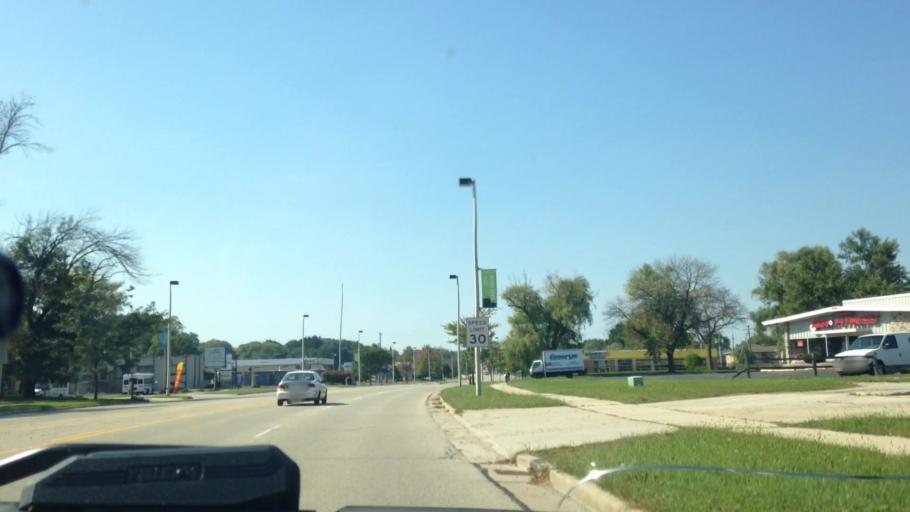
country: US
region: Wisconsin
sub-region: Waukesha County
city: Menomonee Falls
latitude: 43.1774
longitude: -88.0961
